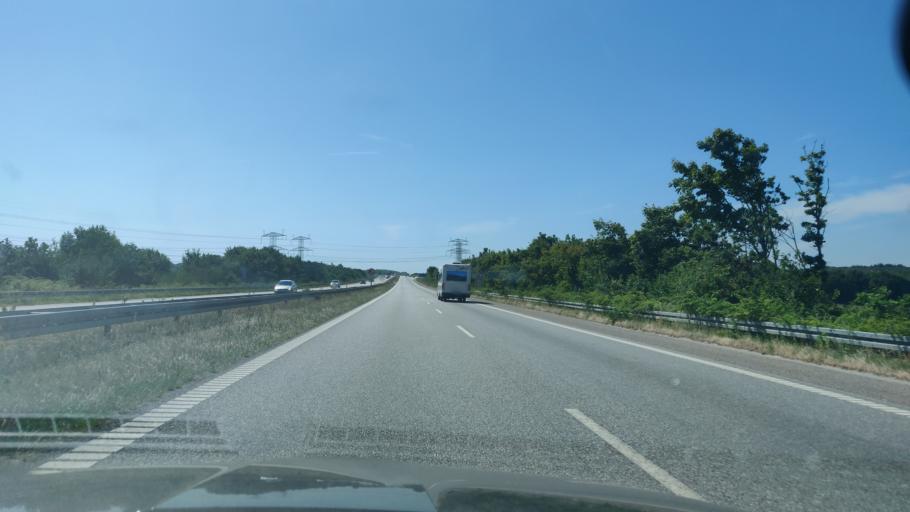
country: DK
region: North Denmark
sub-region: Alborg Kommune
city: Svenstrup
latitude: 56.9583
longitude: 9.8722
